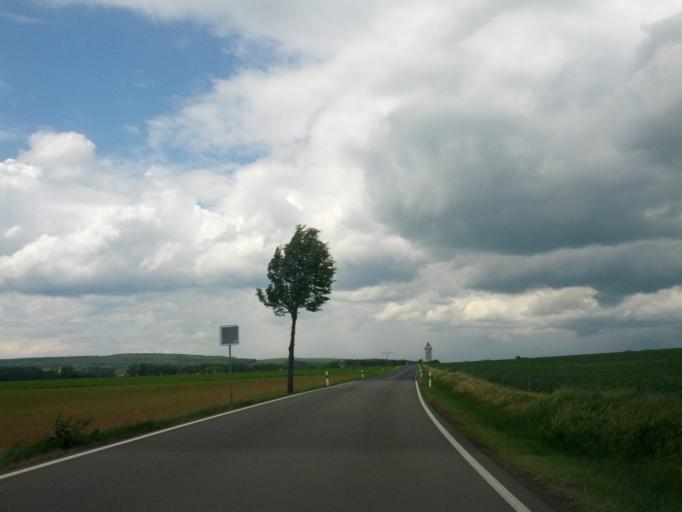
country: DE
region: Thuringia
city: Friedrichswerth
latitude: 51.0071
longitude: 10.5381
